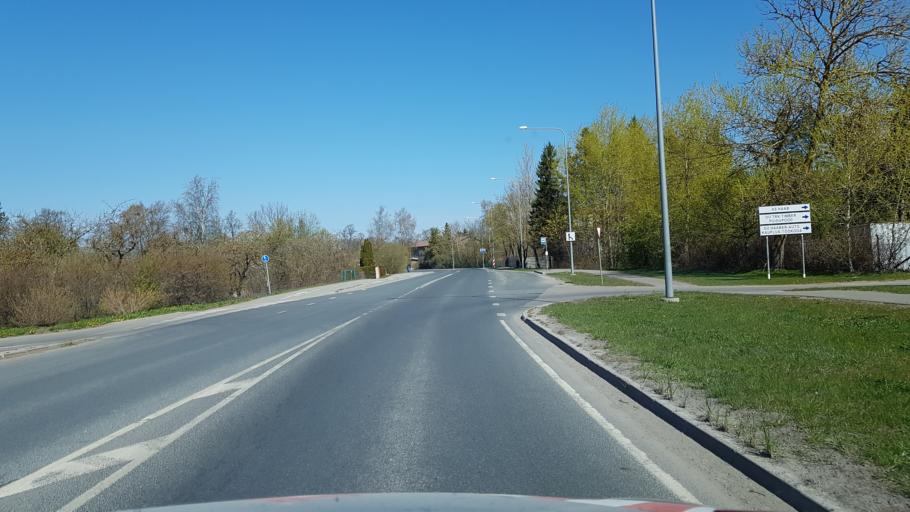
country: EE
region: Harju
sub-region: Viimsi vald
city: Haabneeme
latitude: 59.5076
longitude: 24.8223
